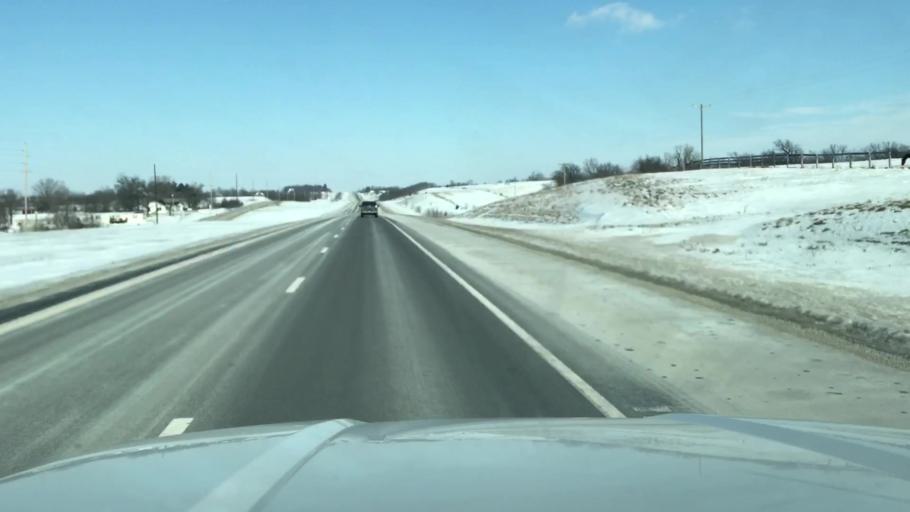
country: US
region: Missouri
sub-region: Nodaway County
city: Maryville
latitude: 40.1868
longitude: -94.8678
